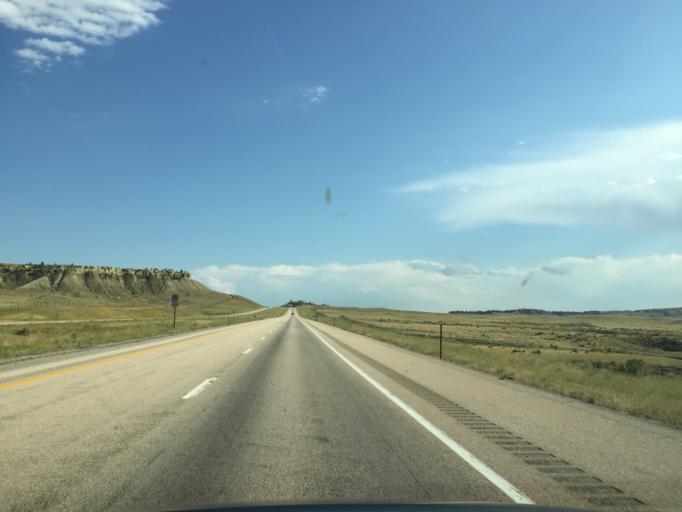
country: US
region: Wyoming
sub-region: Natrona County
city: Bar Nunn
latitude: 43.2710
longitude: -106.3911
